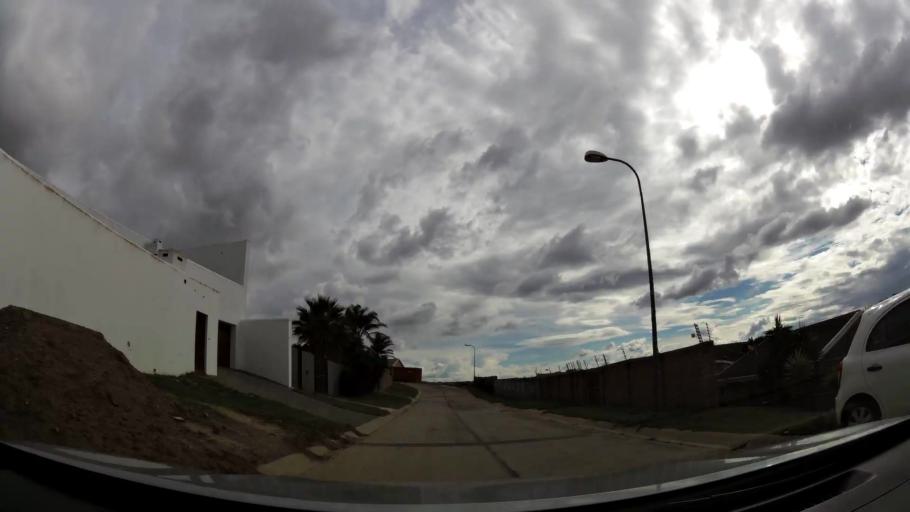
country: ZA
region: Eastern Cape
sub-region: Nelson Mandela Bay Metropolitan Municipality
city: Port Elizabeth
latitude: -33.9313
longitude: 25.5170
